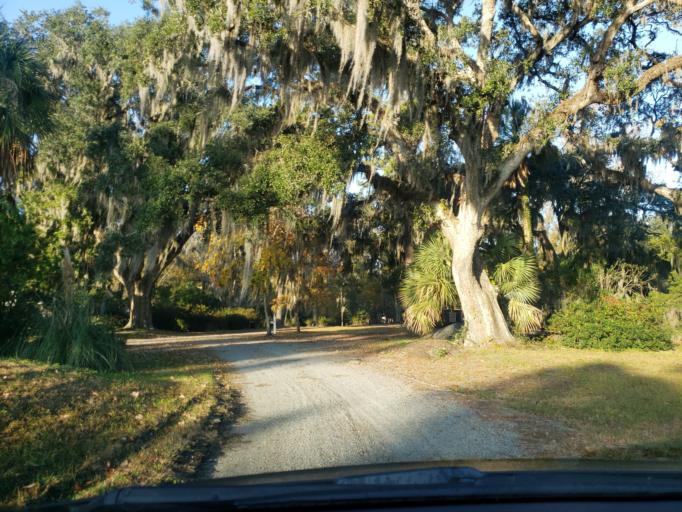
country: US
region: Georgia
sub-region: Chatham County
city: Montgomery
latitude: 31.9824
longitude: -81.1254
